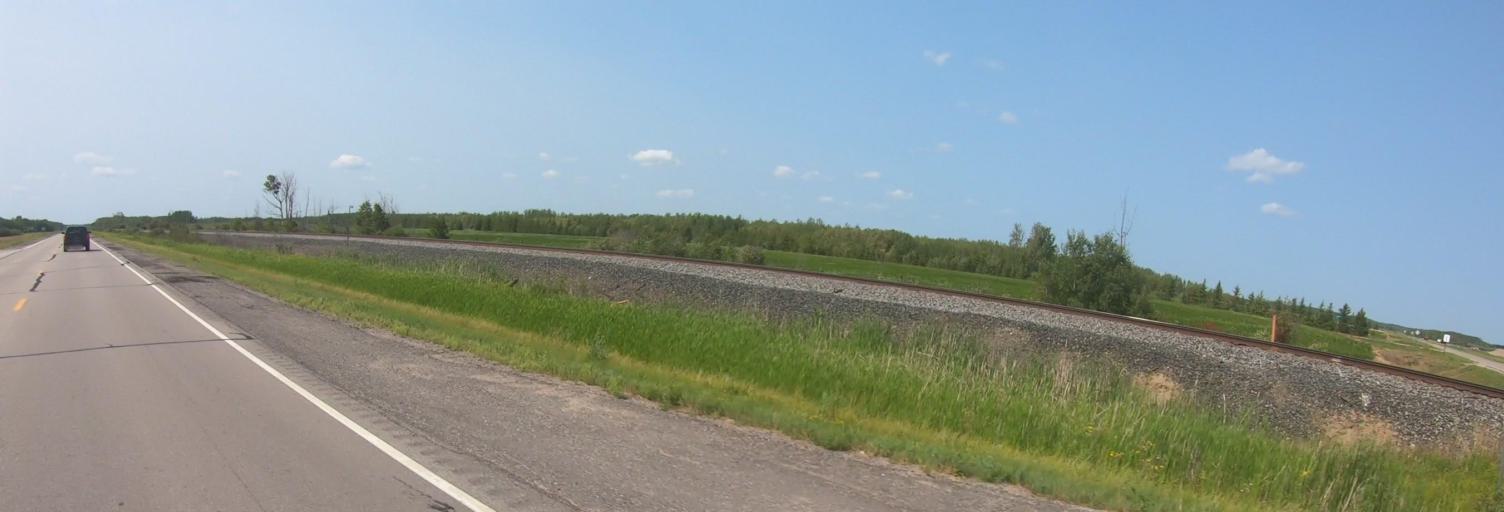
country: US
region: Minnesota
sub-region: Lake of the Woods County
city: Baudette
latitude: 48.7130
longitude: -94.6526
